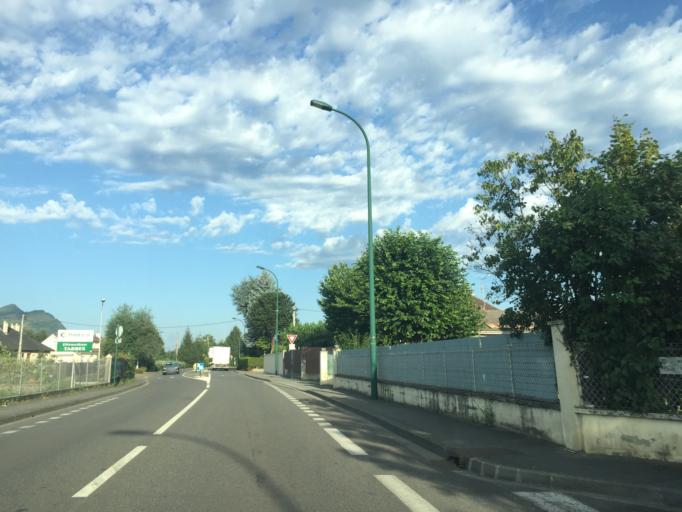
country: FR
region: Midi-Pyrenees
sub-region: Departement des Hautes-Pyrenees
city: Lourdes
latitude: 43.0964
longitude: -0.0246
